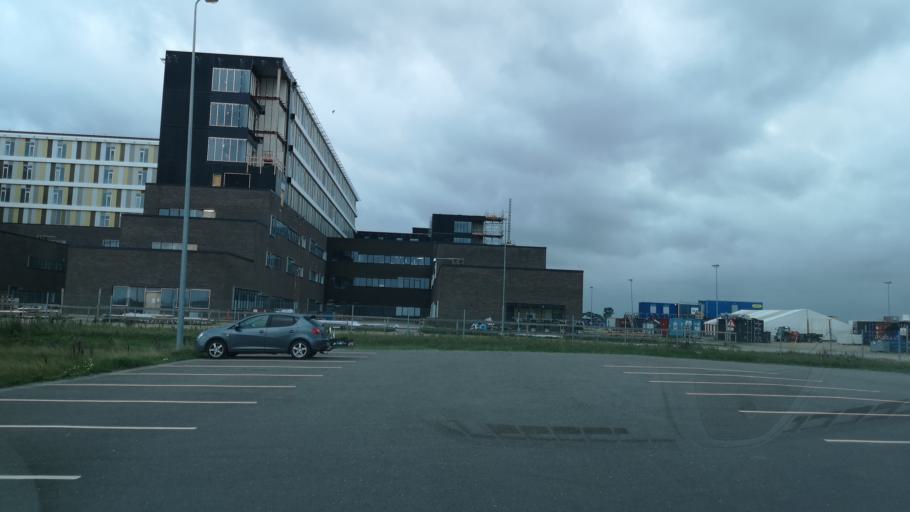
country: DK
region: Central Jutland
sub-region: Herning Kommune
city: Snejbjerg
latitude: 56.1592
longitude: 8.8899
